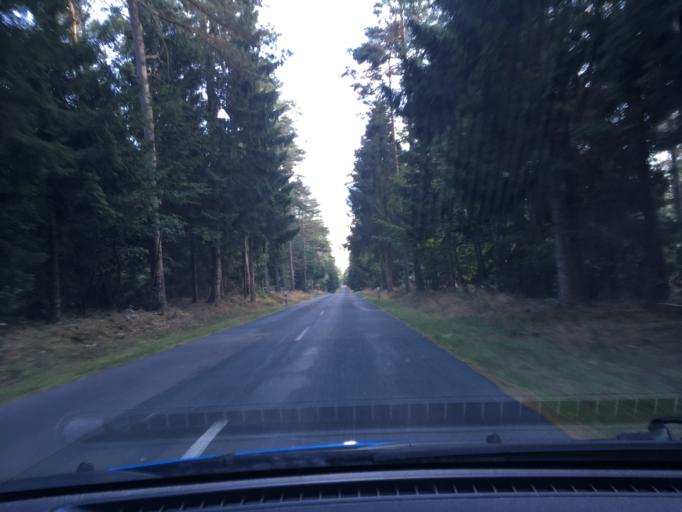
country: DE
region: Lower Saxony
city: Thomasburg
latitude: 53.2473
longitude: 10.7077
